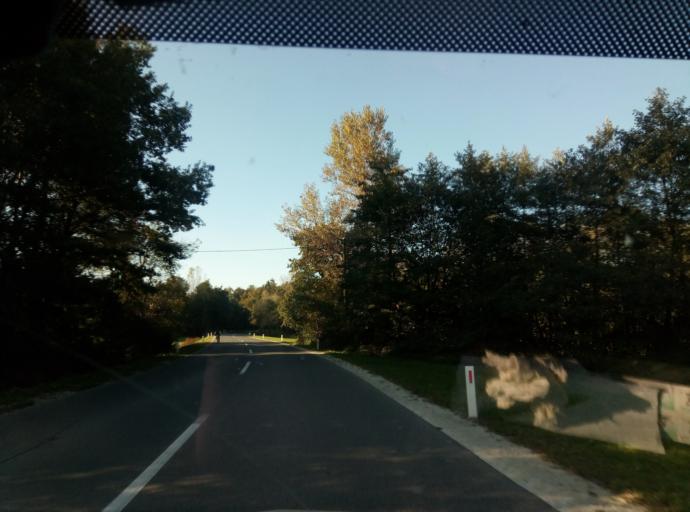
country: SI
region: Medvode
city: Zgornje Pirnice
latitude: 46.1334
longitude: 14.4778
